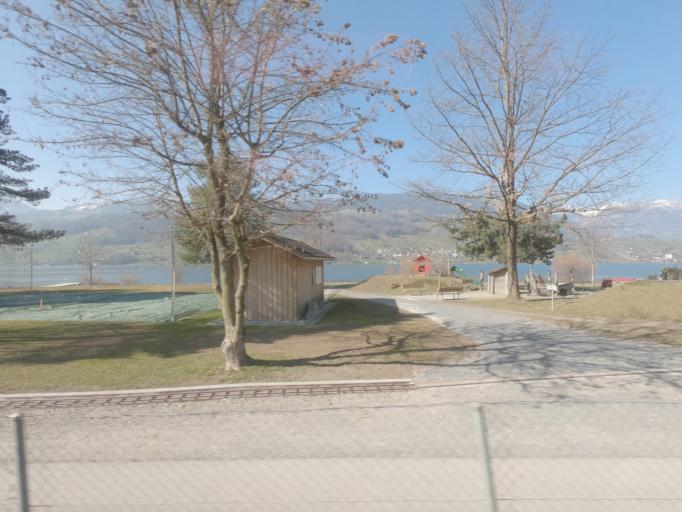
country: CH
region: Obwalden
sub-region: Obwalden
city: Sachseln
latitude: 46.8674
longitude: 8.2326
